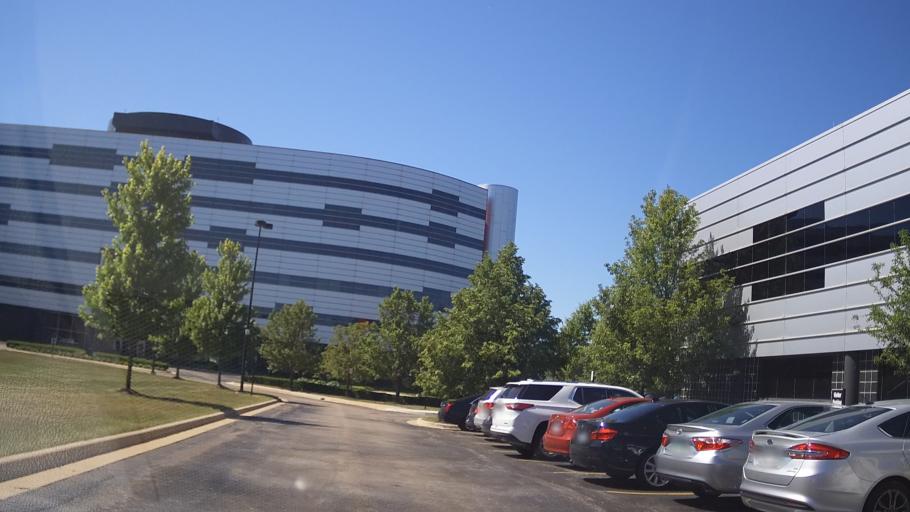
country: US
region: Michigan
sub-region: Oakland County
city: Troy
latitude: 42.6032
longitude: -83.1624
